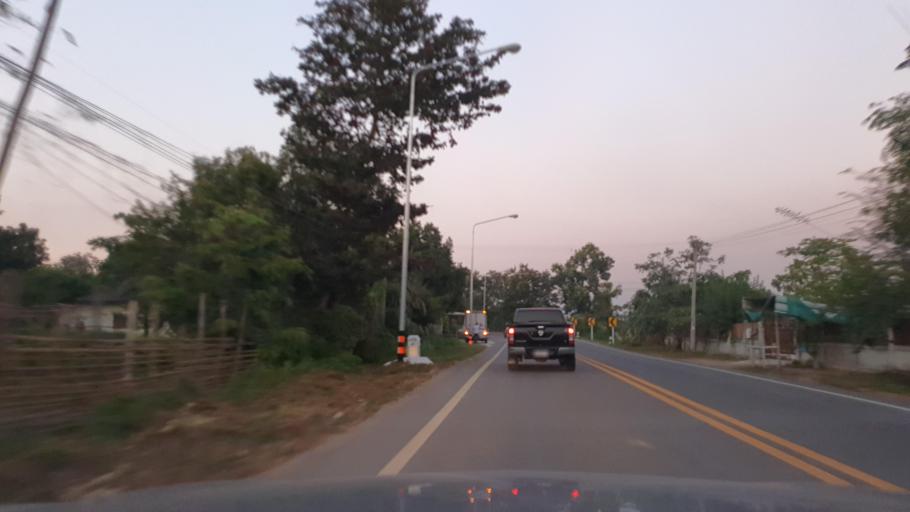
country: TH
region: Phayao
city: Dok Kham Tai
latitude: 19.1431
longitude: 100.0154
